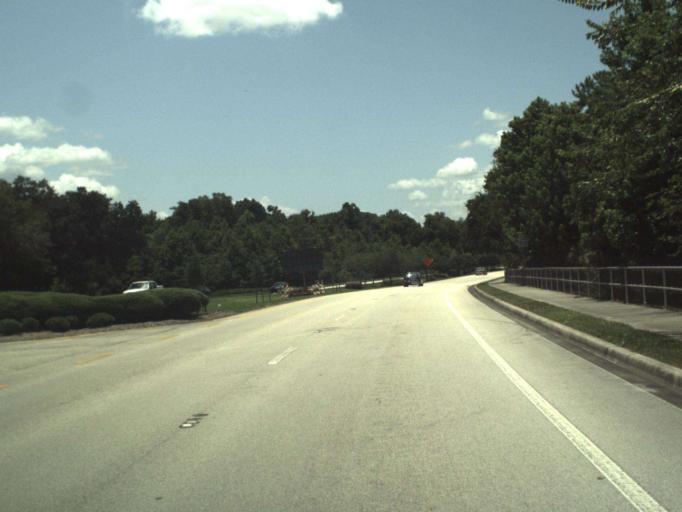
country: US
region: Florida
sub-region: Seminole County
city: Oviedo
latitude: 28.6906
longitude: -81.2551
